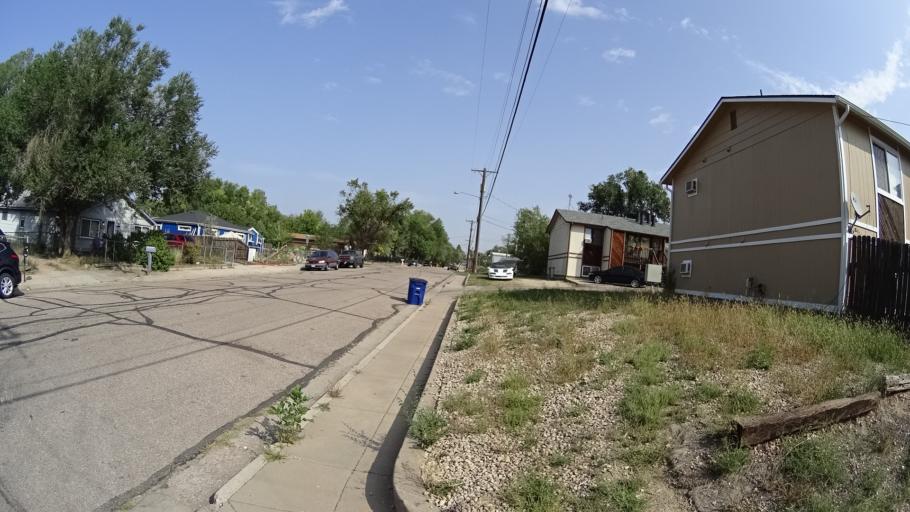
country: US
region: Colorado
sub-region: El Paso County
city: Colorado Springs
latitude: 38.8417
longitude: -104.7780
